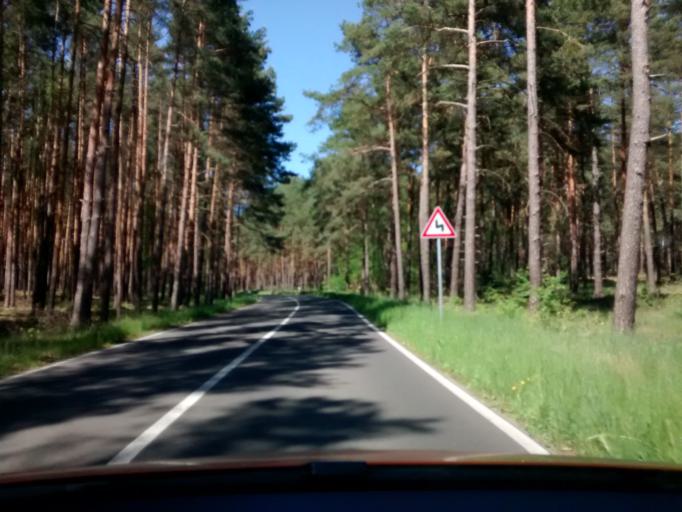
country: DE
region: Brandenburg
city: Wendisch Rietz
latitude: 52.2249
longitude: 13.9995
